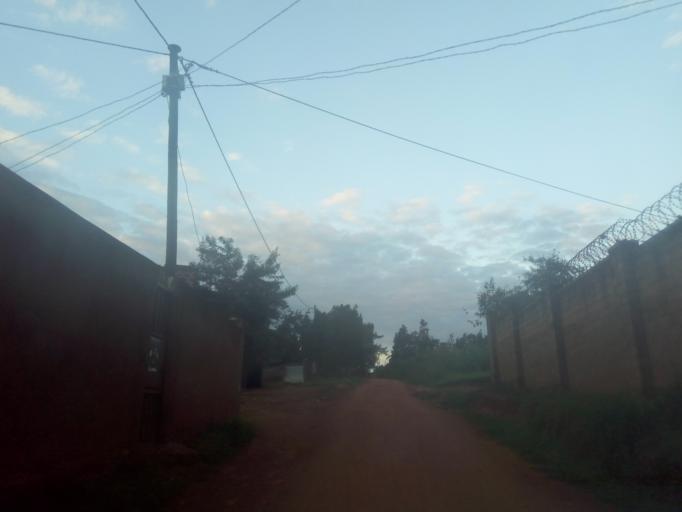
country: UG
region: Central Region
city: Kampala Central Division
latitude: 0.3897
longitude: 32.5640
